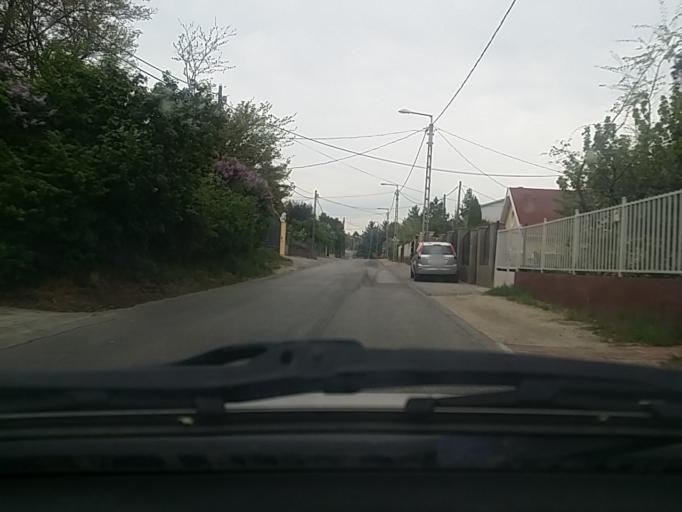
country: HU
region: Budapest
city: Budapest III. keruelet
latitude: 47.5554
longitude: 19.0193
